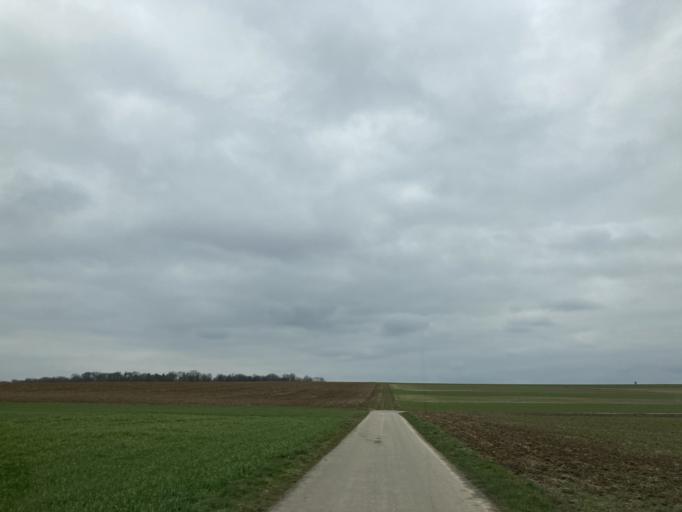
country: DE
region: Baden-Wuerttemberg
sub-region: Tuebingen Region
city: Hirrlingen
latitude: 48.4256
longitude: 8.8982
